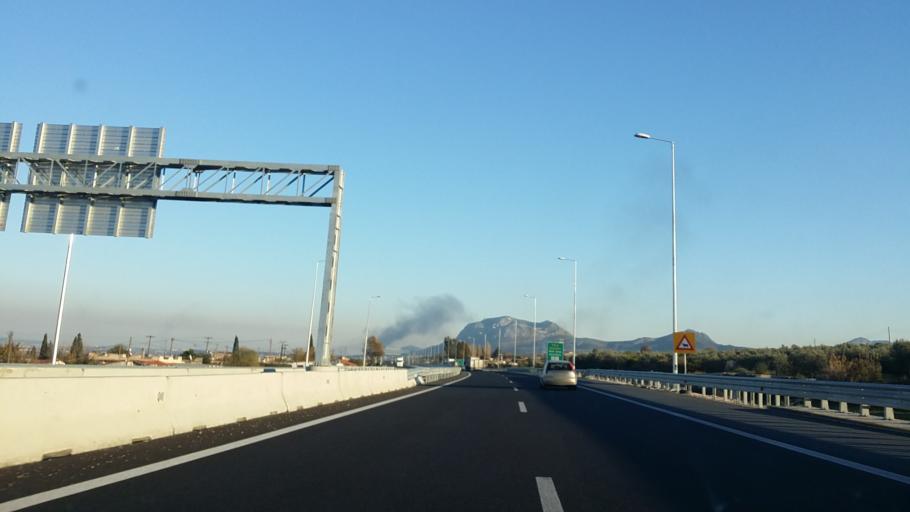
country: GR
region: Peloponnese
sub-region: Nomos Korinthias
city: Zevgolateio
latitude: 37.9268
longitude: 22.7940
